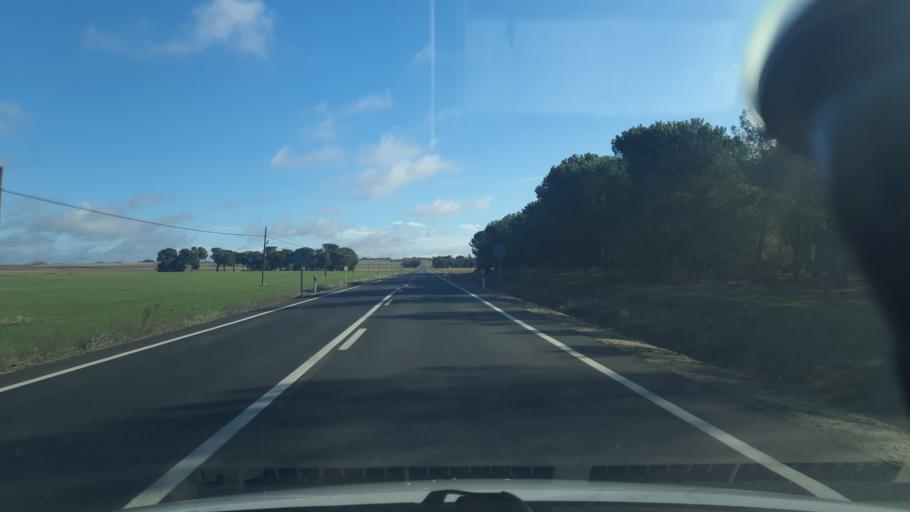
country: ES
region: Castille and Leon
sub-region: Provincia de Segovia
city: Martin Munoz de la Dehesa
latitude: 41.0464
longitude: -4.6596
